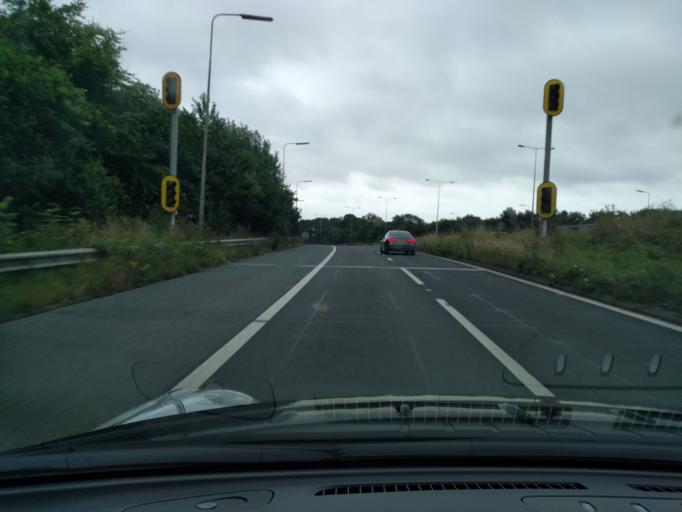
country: GB
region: England
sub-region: Borough of Wigan
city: Ashton in Makerfield
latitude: 53.4700
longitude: -2.6323
